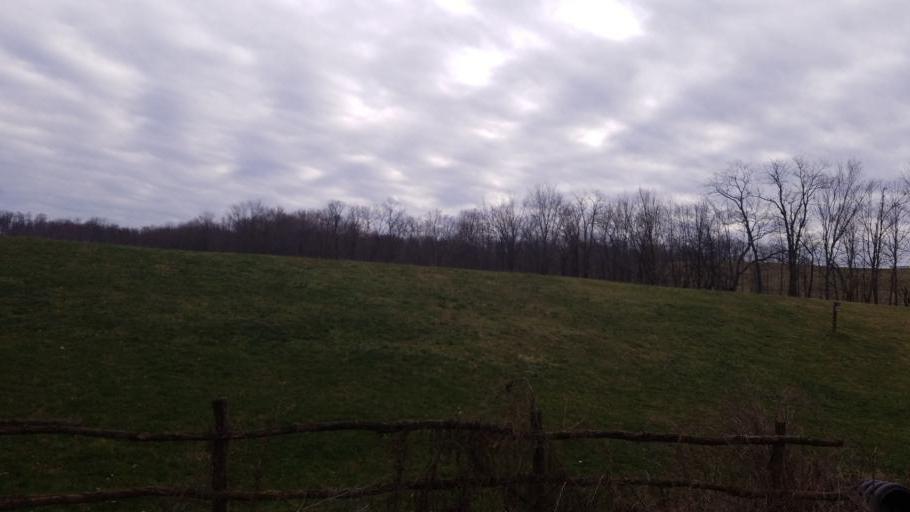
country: US
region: Ohio
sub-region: Knox County
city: Fredericktown
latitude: 40.5181
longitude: -82.4061
